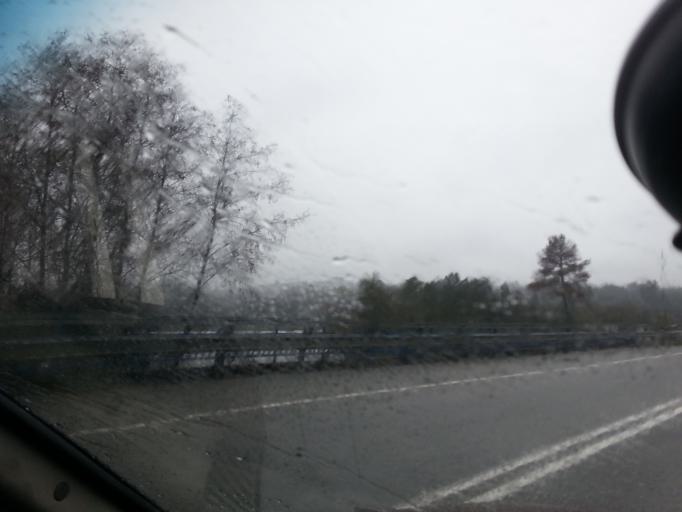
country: PT
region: Guarda
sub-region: Fornos de Algodres
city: Fornos de Algodres
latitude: 40.6064
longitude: -7.5882
